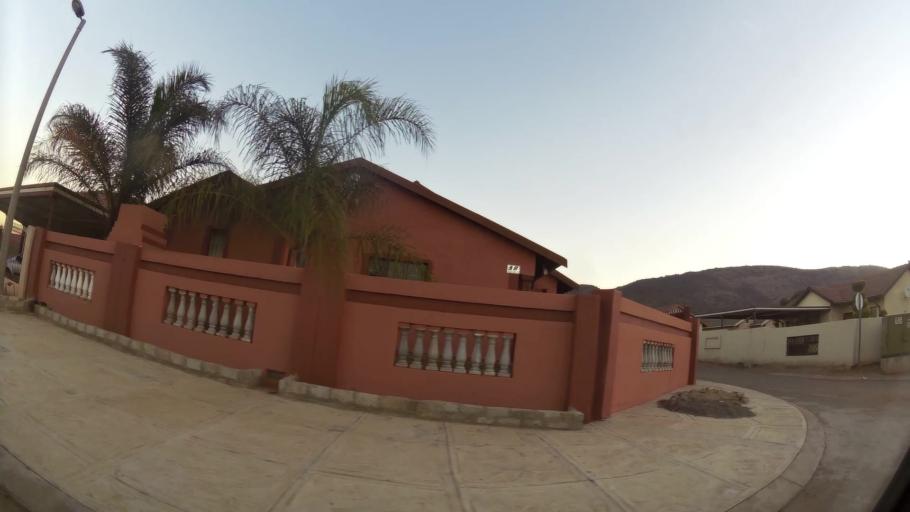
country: ZA
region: North-West
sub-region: Bojanala Platinum District Municipality
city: Rustenburg
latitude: -25.6438
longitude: 27.2033
